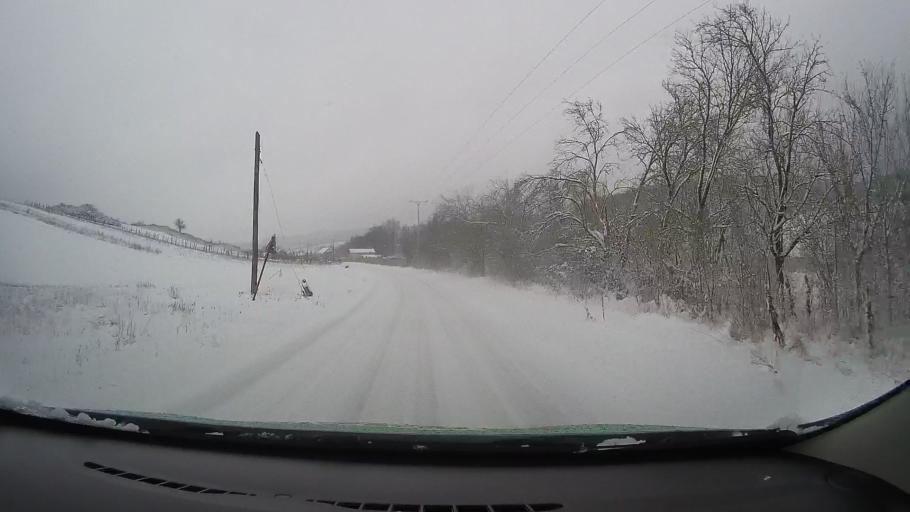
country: RO
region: Hunedoara
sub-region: Comuna Carjiti
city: Carjiti
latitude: 45.8324
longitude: 22.8412
